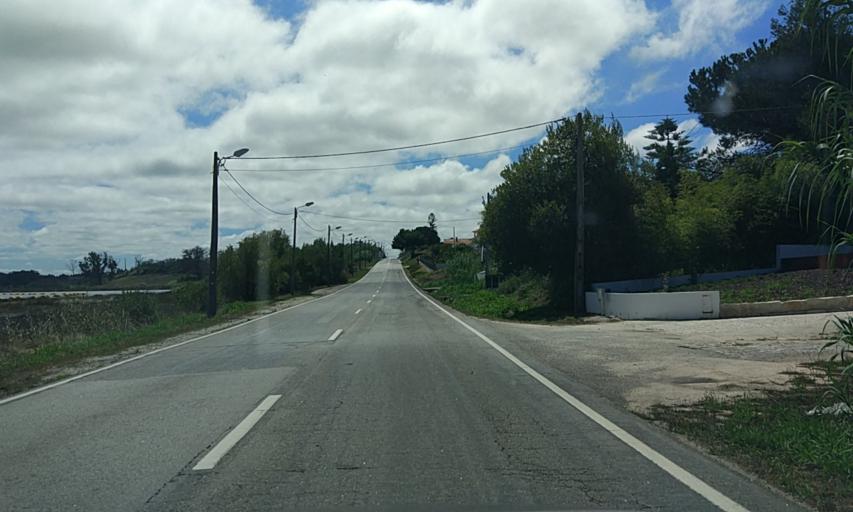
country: PT
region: Aveiro
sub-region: Vagos
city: Vagos
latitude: 40.5684
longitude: -8.6826
